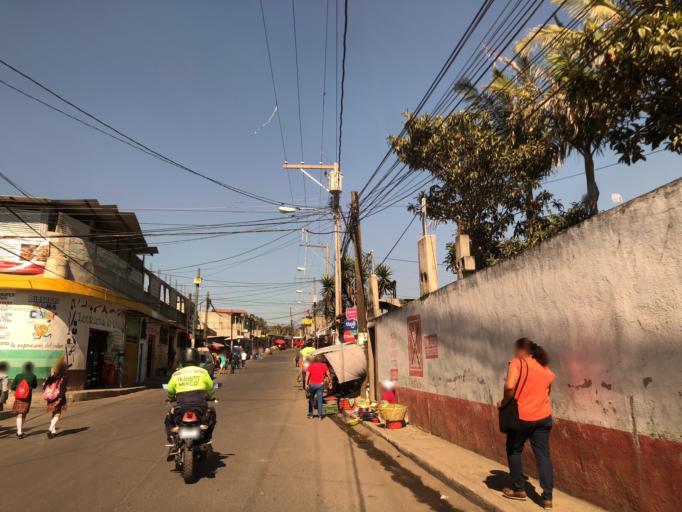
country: GT
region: Guatemala
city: Mixco
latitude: 14.6125
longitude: -90.5765
